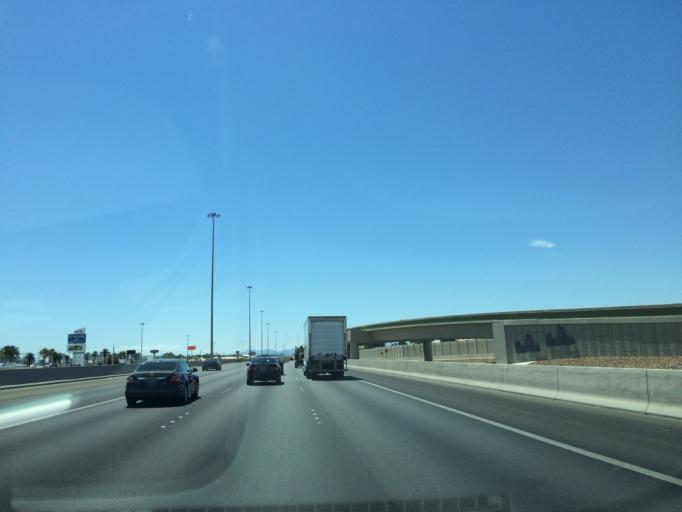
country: US
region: Nevada
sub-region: Clark County
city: Las Vegas
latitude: 36.2618
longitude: -115.2527
